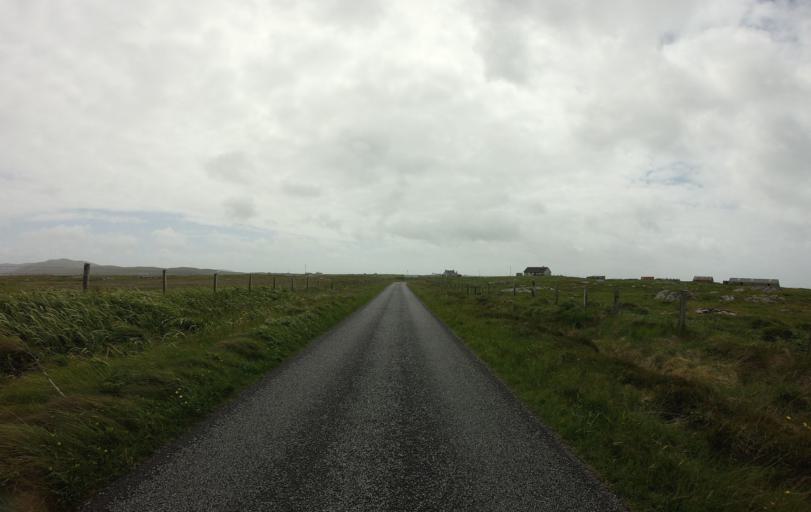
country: GB
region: Scotland
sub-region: Eilean Siar
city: Isle of South Uist
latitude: 57.2552
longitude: -7.4046
